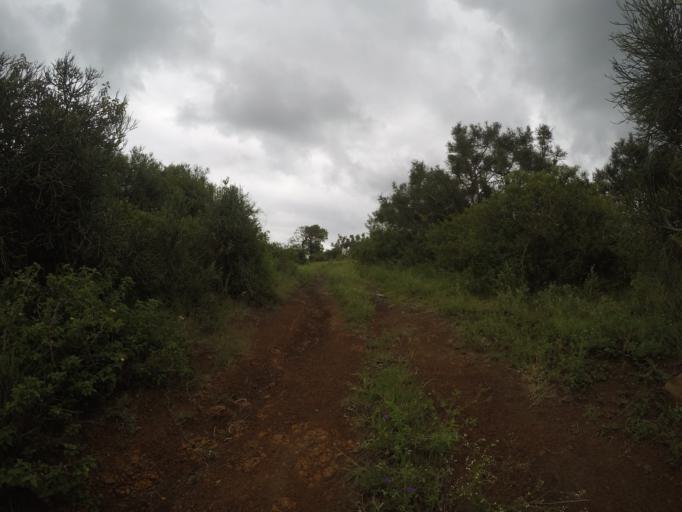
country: ZA
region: KwaZulu-Natal
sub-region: uThungulu District Municipality
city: Empangeni
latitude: -28.5864
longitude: 31.8661
